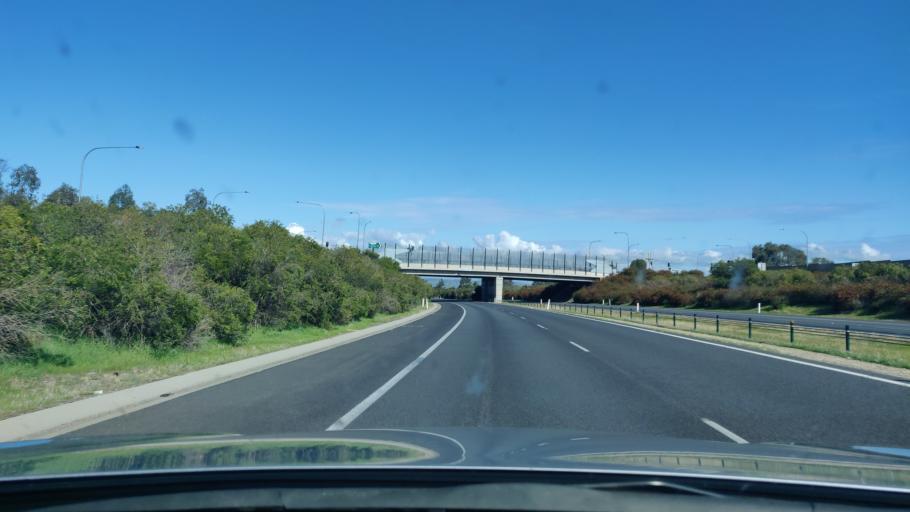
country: AU
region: New South Wales
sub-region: Albury Municipality
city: Albury
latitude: -36.0742
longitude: 146.9289
